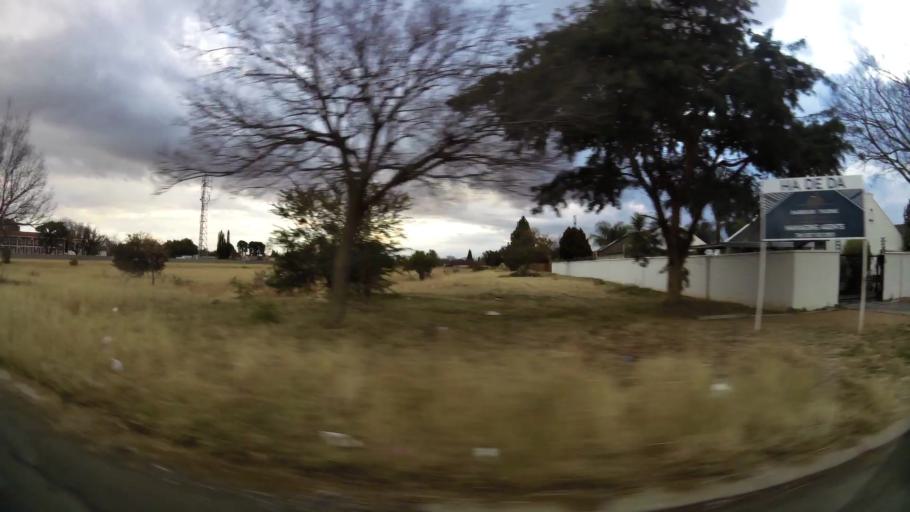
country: ZA
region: Orange Free State
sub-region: Lejweleputswa District Municipality
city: Welkom
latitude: -27.9534
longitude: 26.7257
